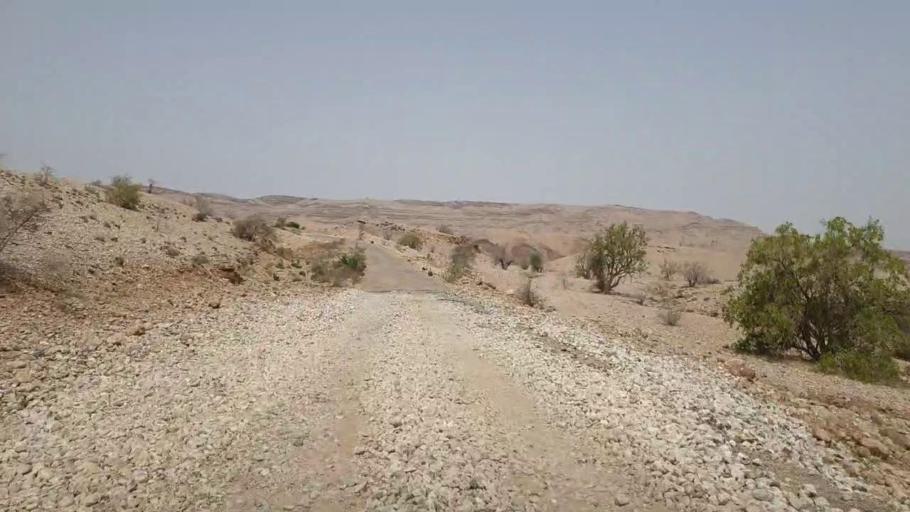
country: PK
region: Sindh
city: Sann
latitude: 25.8865
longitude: 67.9079
